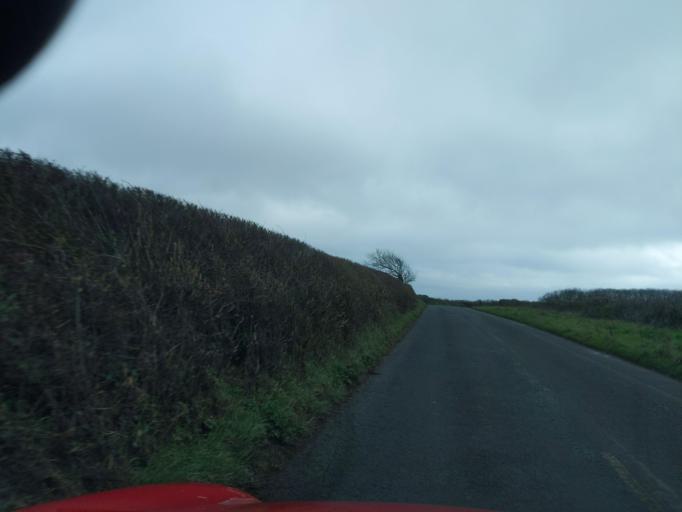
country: GB
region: England
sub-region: Devon
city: Wembury
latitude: 50.3349
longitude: -4.0947
